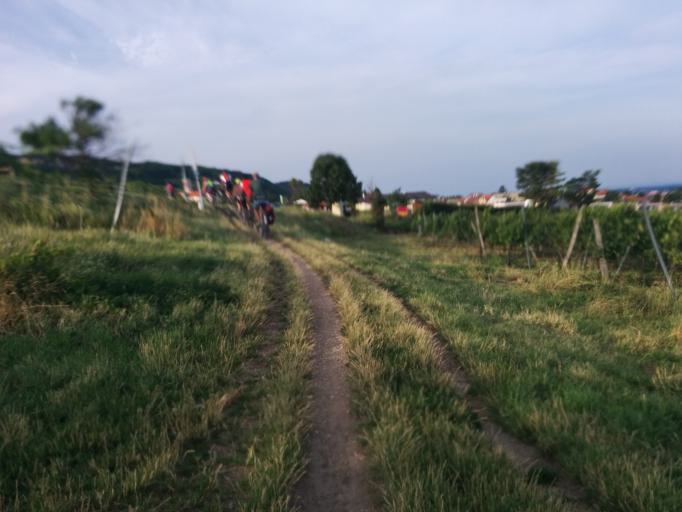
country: AT
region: Lower Austria
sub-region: Politischer Bezirk Modling
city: Gumpoldskirchen
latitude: 48.0412
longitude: 16.2708
